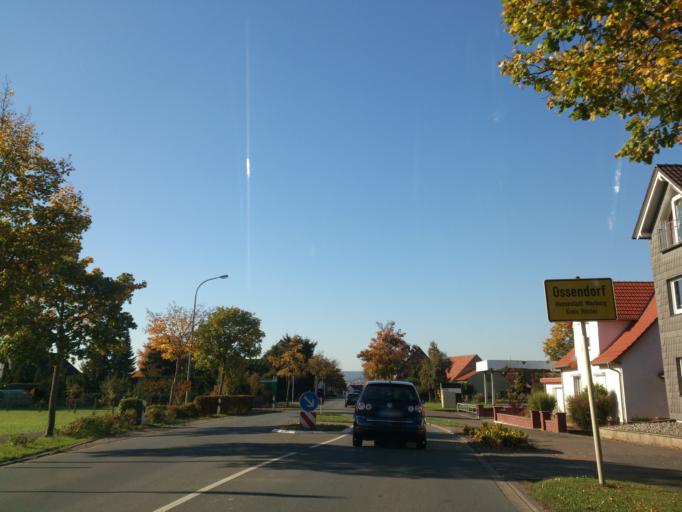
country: DE
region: North Rhine-Westphalia
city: Warburg
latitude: 51.5090
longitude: 9.0913
